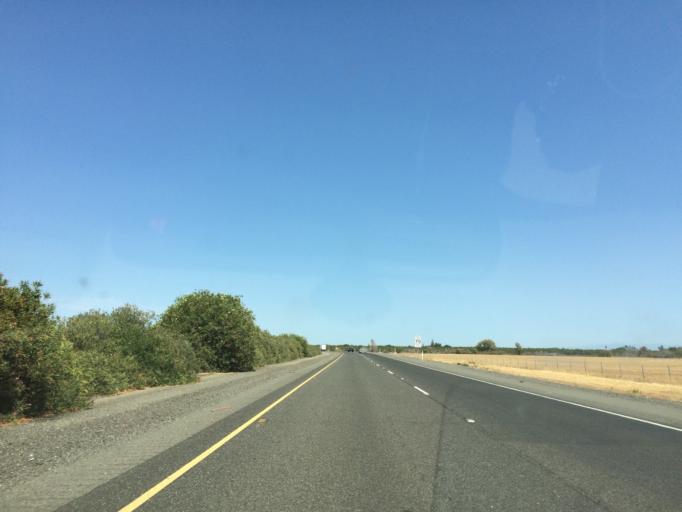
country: US
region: California
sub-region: Glenn County
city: Willows
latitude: 39.6284
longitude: -122.2044
